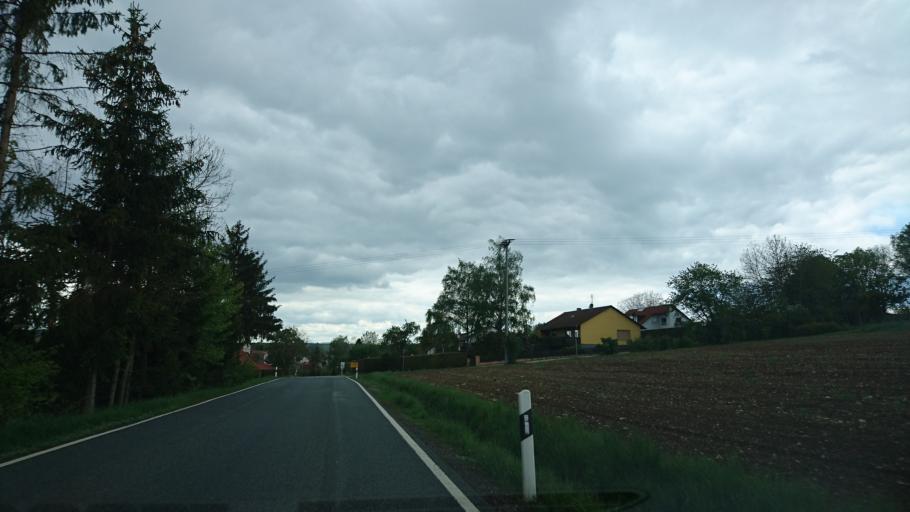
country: DE
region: Bavaria
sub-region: Regierungsbezirk Mittelfranken
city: Nennslingen
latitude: 49.0472
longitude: 11.1404
